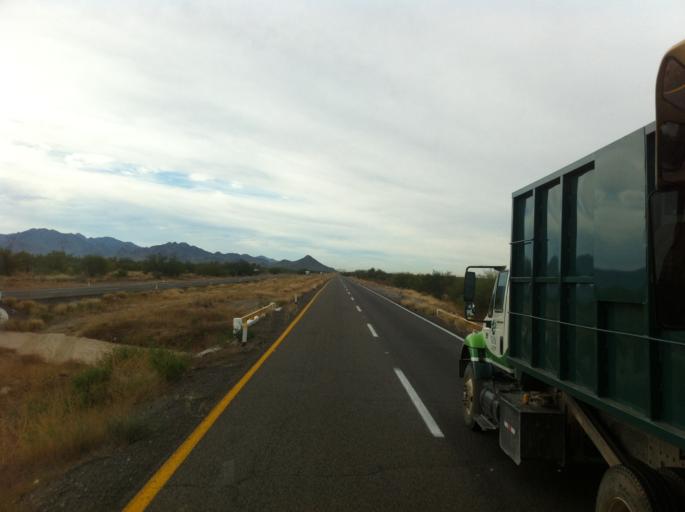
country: MX
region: Sonora
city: Hermosillo
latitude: 28.7143
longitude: -110.9833
